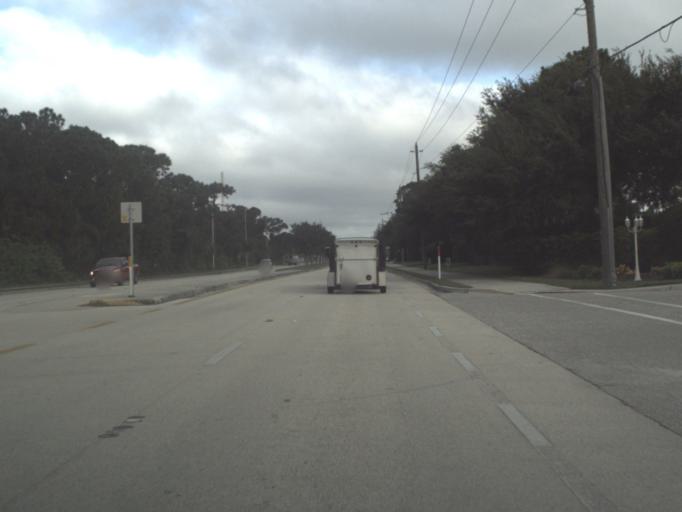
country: US
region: Florida
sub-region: Sarasota County
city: Englewood
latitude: 26.9821
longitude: -82.3606
